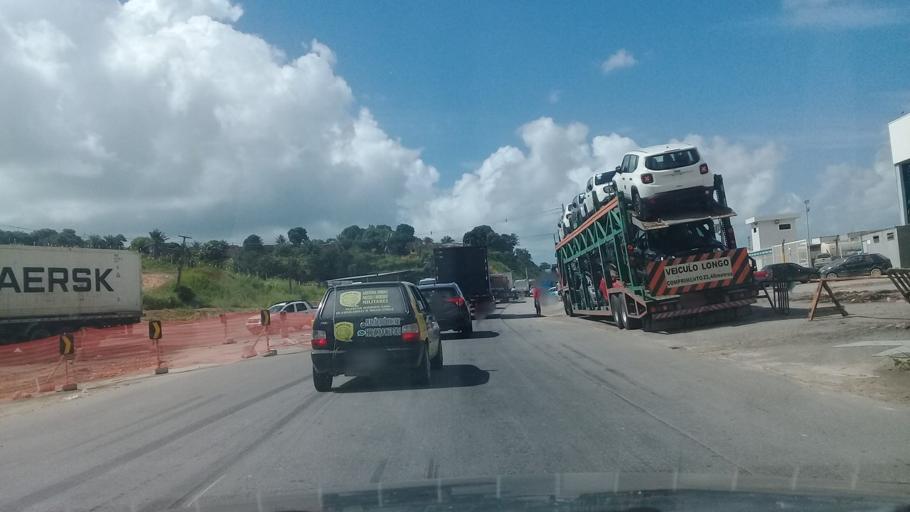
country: BR
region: Pernambuco
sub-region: Jaboatao Dos Guararapes
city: Jaboatao
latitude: -8.1479
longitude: -34.9444
